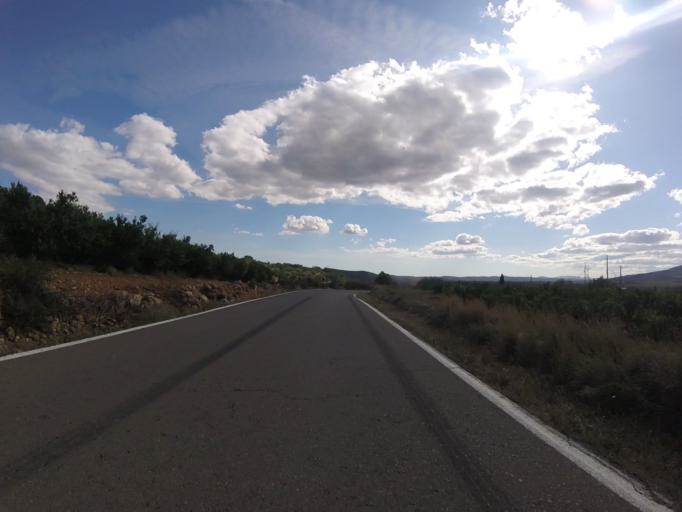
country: ES
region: Valencia
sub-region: Provincia de Castello
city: Cuevas de Vinroma
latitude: 40.3718
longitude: 0.1161
